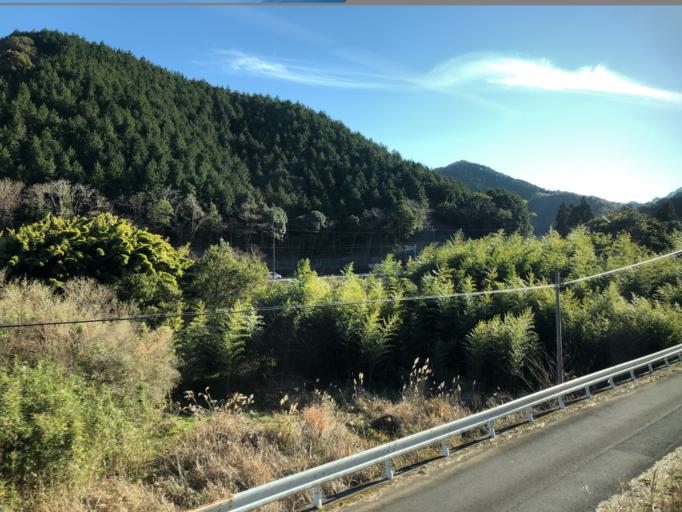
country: JP
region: Kochi
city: Nakamura
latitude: 33.1208
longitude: 133.1176
